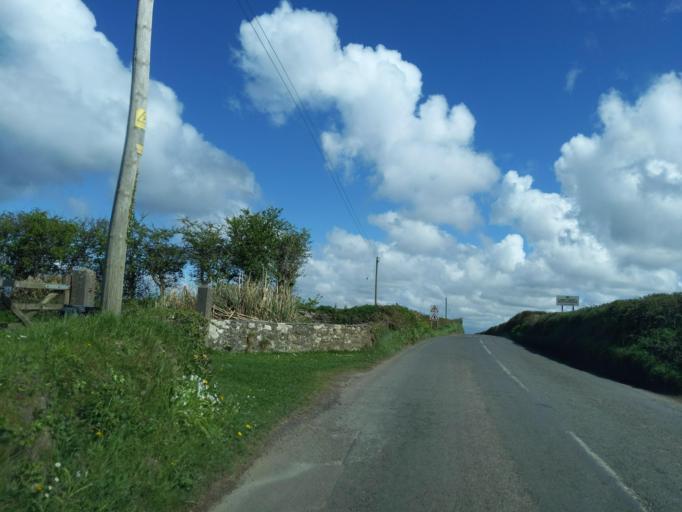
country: GB
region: England
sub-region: Cornwall
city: Wadebridge
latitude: 50.5733
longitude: -4.8342
